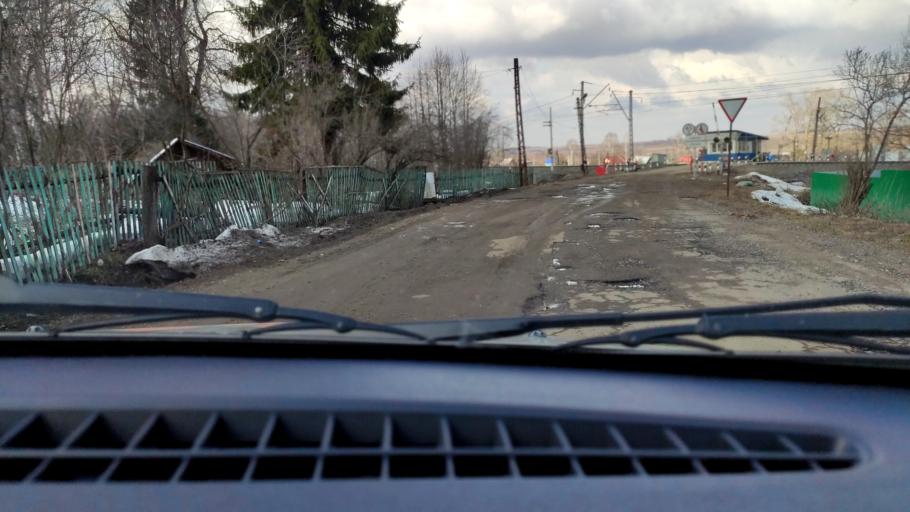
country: RU
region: Bashkortostan
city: Kudeyevskiy
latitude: 54.8658
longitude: 56.7423
